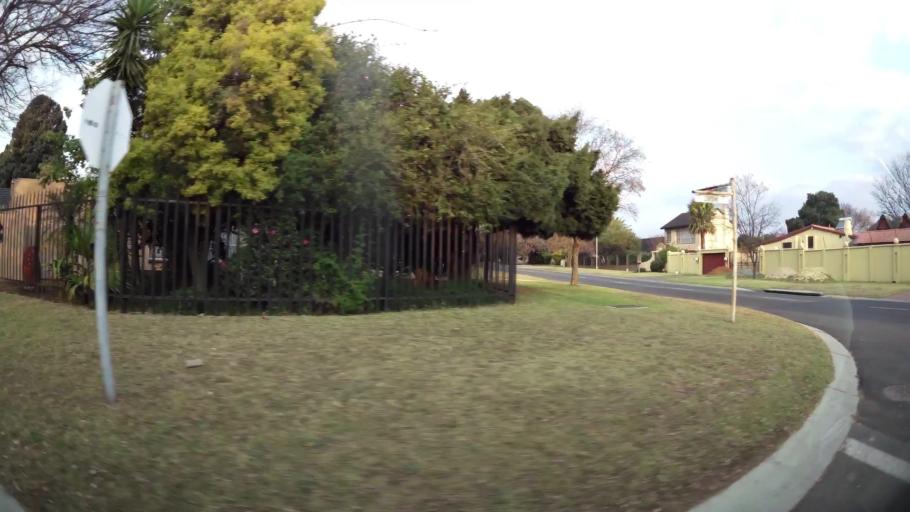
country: ZA
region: Gauteng
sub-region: Ekurhuleni Metropolitan Municipality
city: Benoni
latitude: -26.1531
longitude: 28.2957
